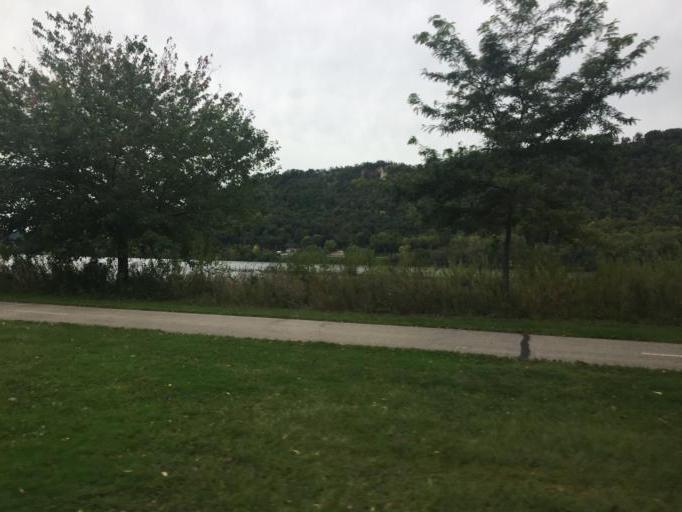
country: US
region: Minnesota
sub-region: Winona County
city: Winona
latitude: 44.0401
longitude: -91.6394
